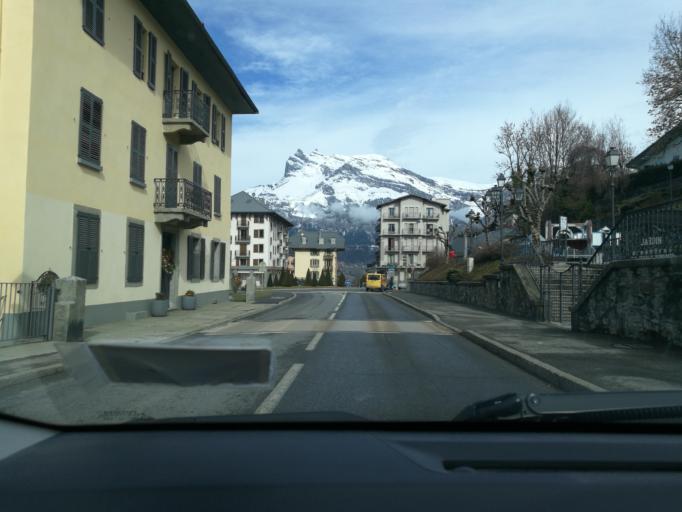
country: FR
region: Rhone-Alpes
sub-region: Departement de la Haute-Savoie
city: Saint-Gervais-les-Bains
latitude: 45.8938
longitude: 6.7109
